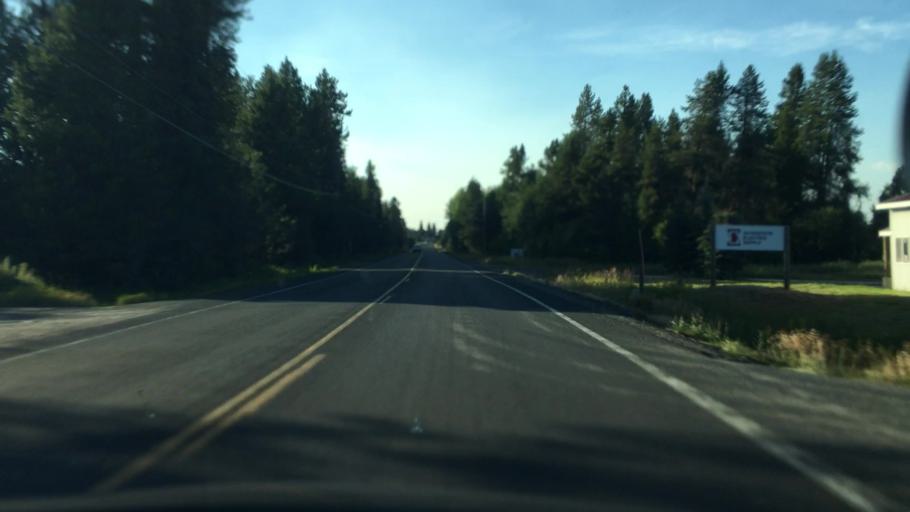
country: US
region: Idaho
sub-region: Valley County
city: McCall
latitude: 44.8253
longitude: -116.0792
